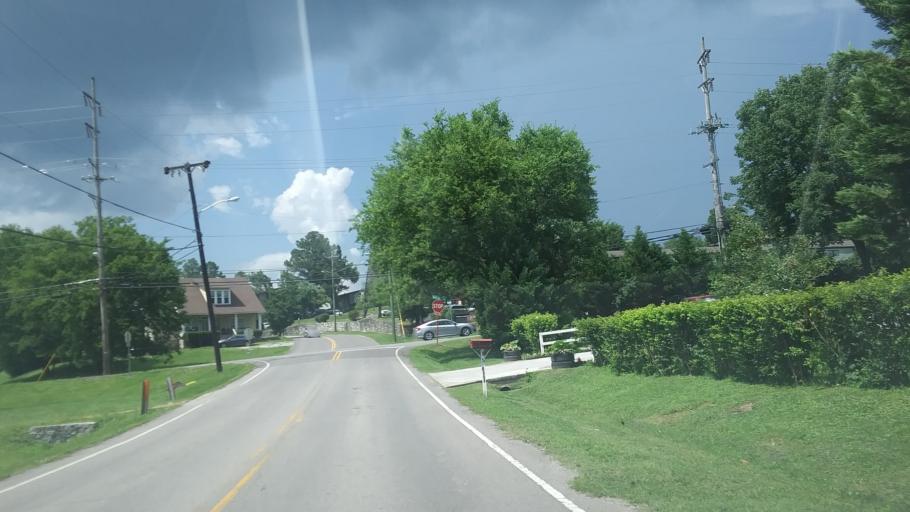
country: US
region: Tennessee
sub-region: Davidson County
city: Oak Hill
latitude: 36.0790
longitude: -86.7145
